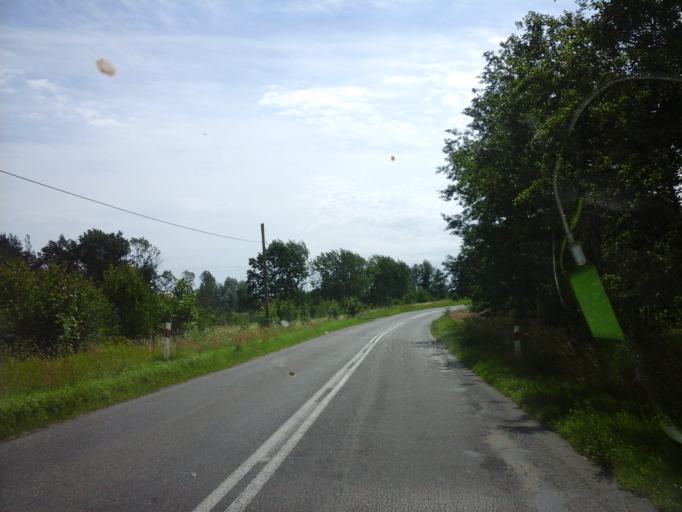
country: PL
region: West Pomeranian Voivodeship
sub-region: Powiat choszczenski
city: Bierzwnik
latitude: 53.0260
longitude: 15.6879
